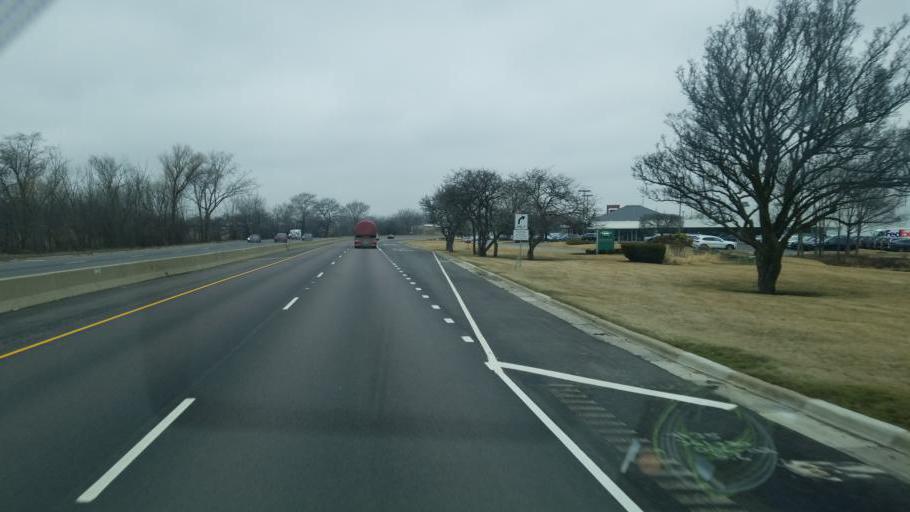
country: US
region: Illinois
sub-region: Lake County
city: Knollwood
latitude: 42.2752
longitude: -87.8683
